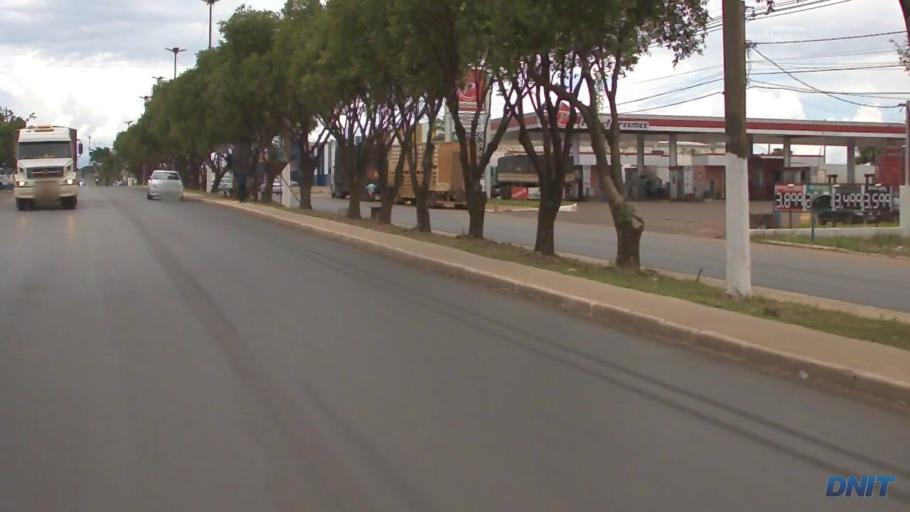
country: BR
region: Mato Grosso
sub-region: Varzea Grande
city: Varzea Grande
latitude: -15.6441
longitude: -56.1825
